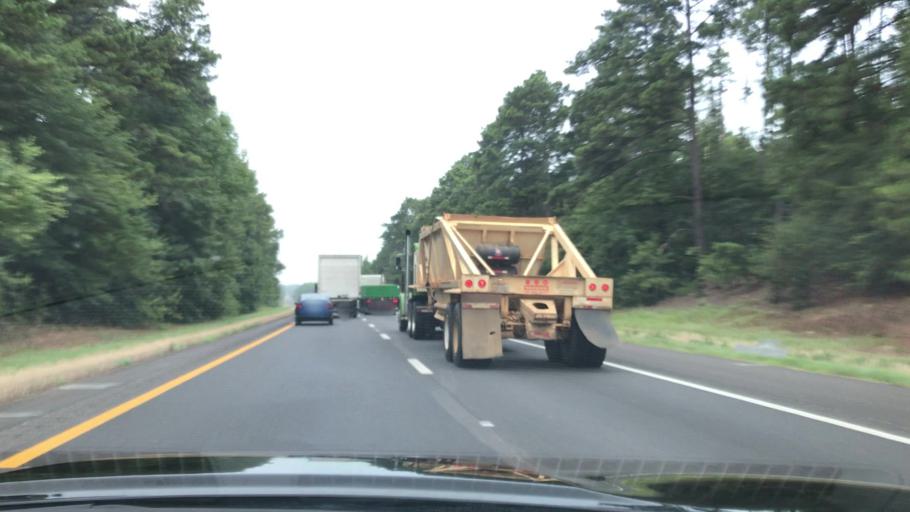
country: US
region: Texas
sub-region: Harrison County
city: Marshall
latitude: 32.4884
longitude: -94.4335
